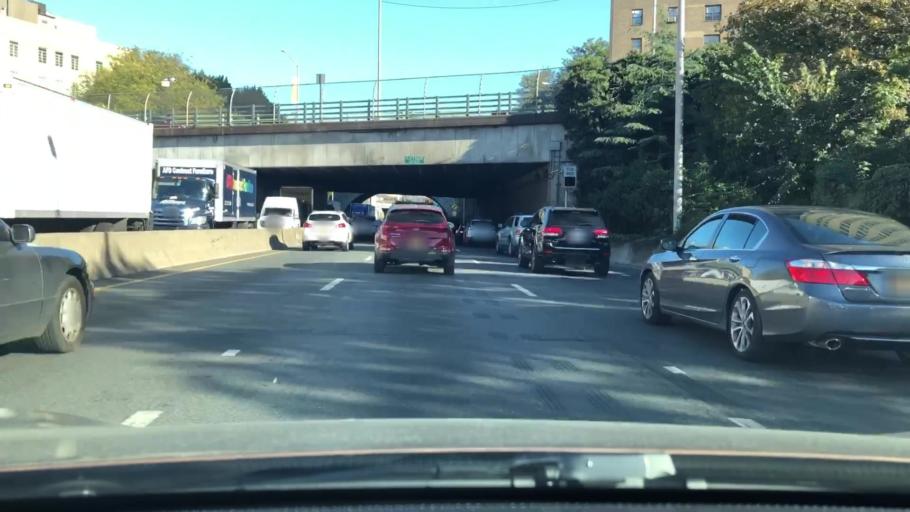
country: US
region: New York
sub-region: Bronx
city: The Bronx
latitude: 40.8437
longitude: -73.8956
